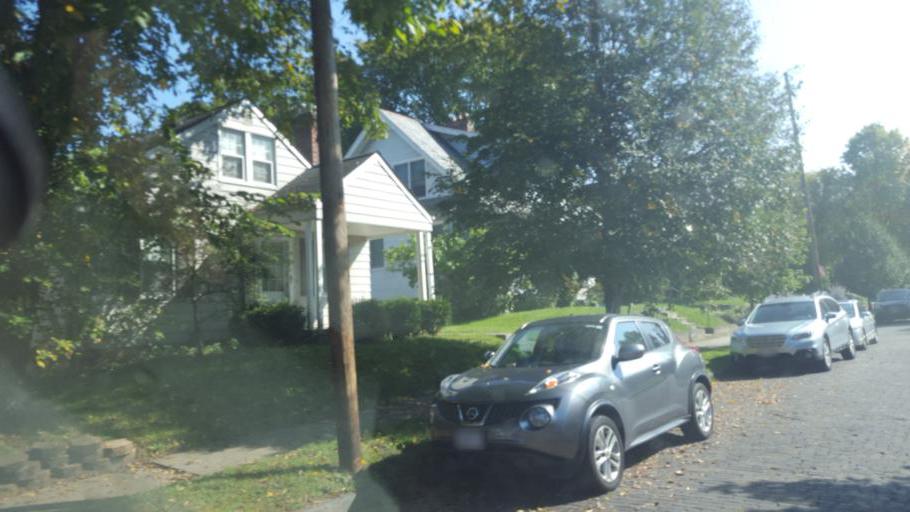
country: US
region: Ohio
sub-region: Franklin County
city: Grandview Heights
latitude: 40.0269
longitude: -83.0200
